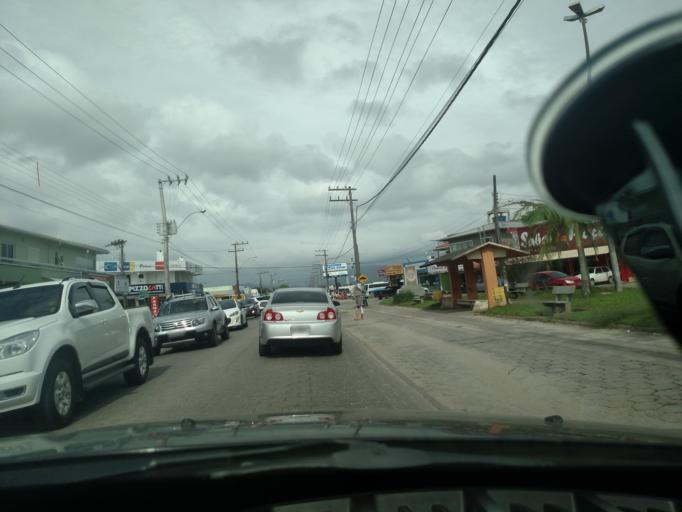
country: BR
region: Santa Catarina
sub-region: Porto Belo
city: Porto Belo
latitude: -27.1597
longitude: -48.5708
